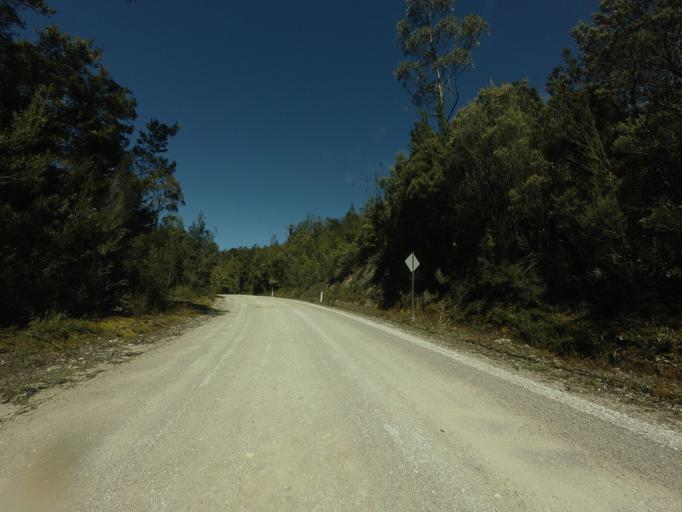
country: AU
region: Tasmania
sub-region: Huon Valley
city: Geeveston
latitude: -42.8288
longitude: 146.3868
